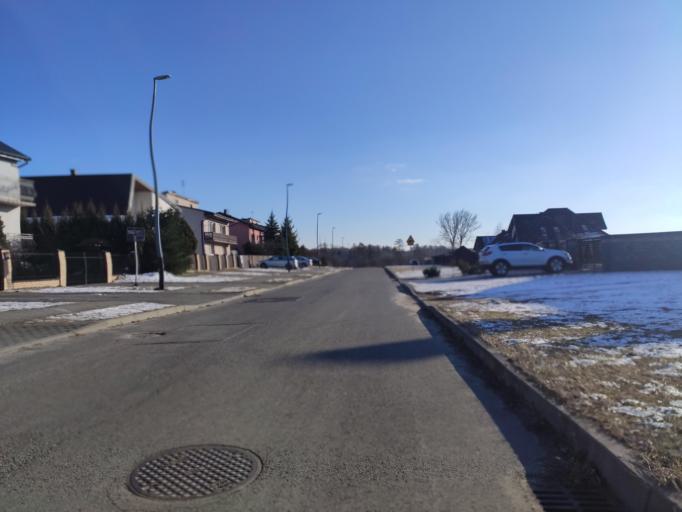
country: PL
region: Lublin Voivodeship
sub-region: Powiat lubartowski
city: Kock
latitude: 51.6403
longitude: 22.4294
